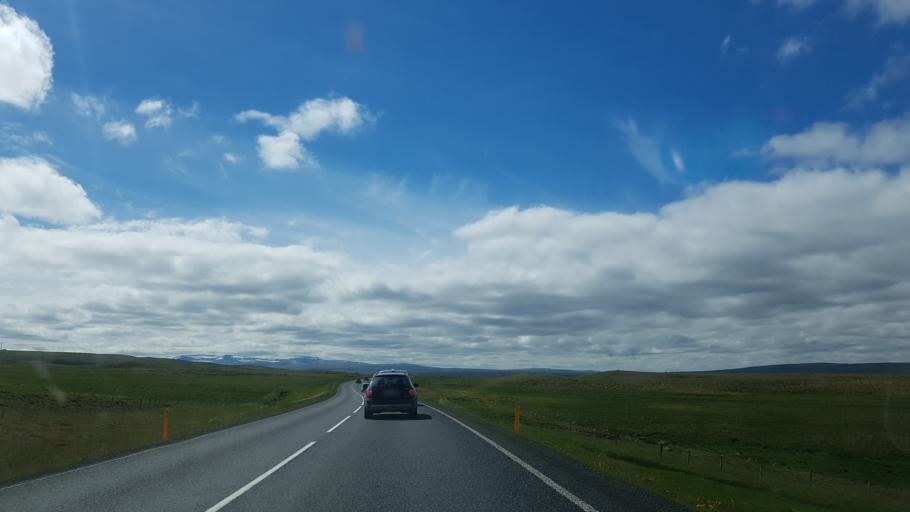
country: IS
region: West
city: Borgarnes
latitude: 65.2858
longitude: -21.0439
